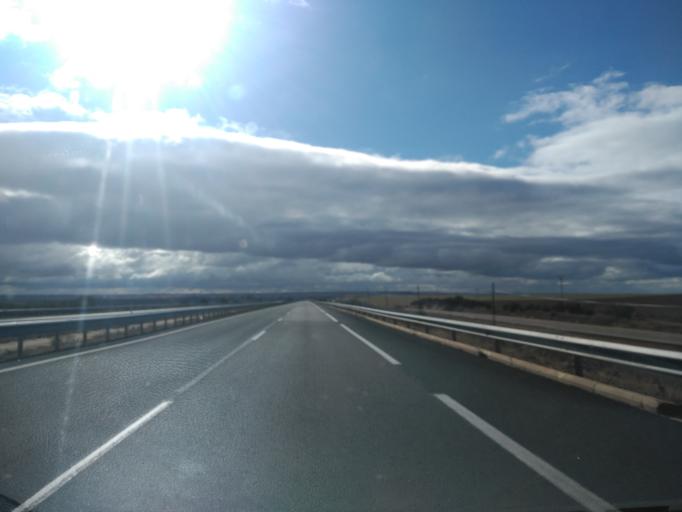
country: ES
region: Castille and Leon
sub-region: Provincia de Palencia
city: Marcilla de Campos
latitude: 42.2924
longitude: -4.3998
